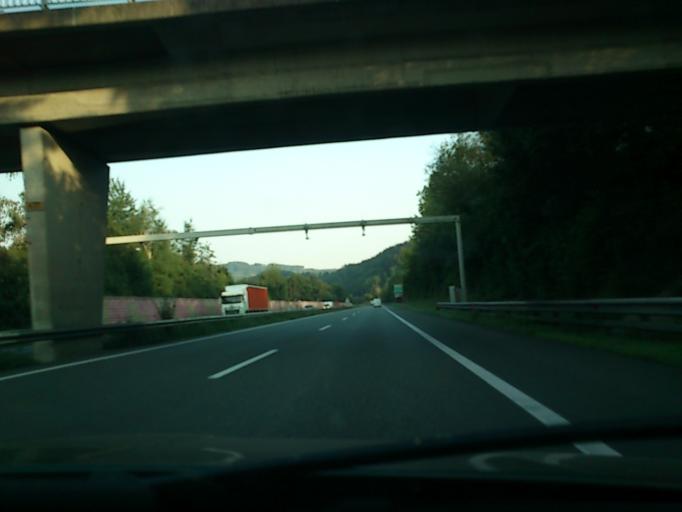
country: AT
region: Styria
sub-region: Politischer Bezirk Graz-Umgebung
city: Deutschfeistritz
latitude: 47.2140
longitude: 15.3064
